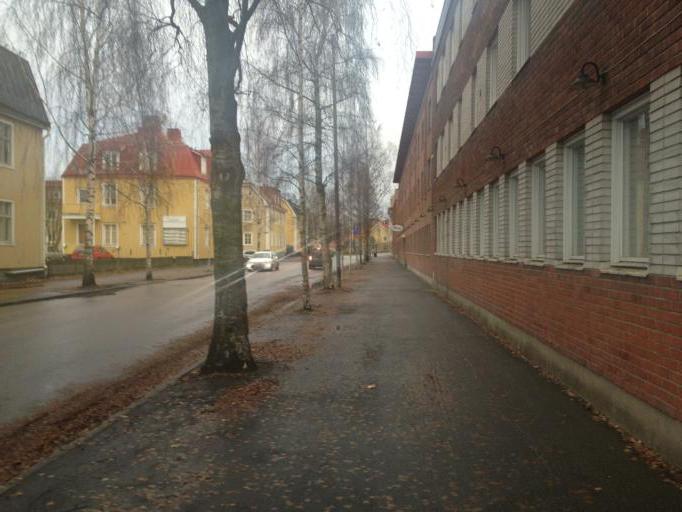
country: SE
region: Vaesterbotten
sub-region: Umea Kommun
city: Umea
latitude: 63.8221
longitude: 20.2790
